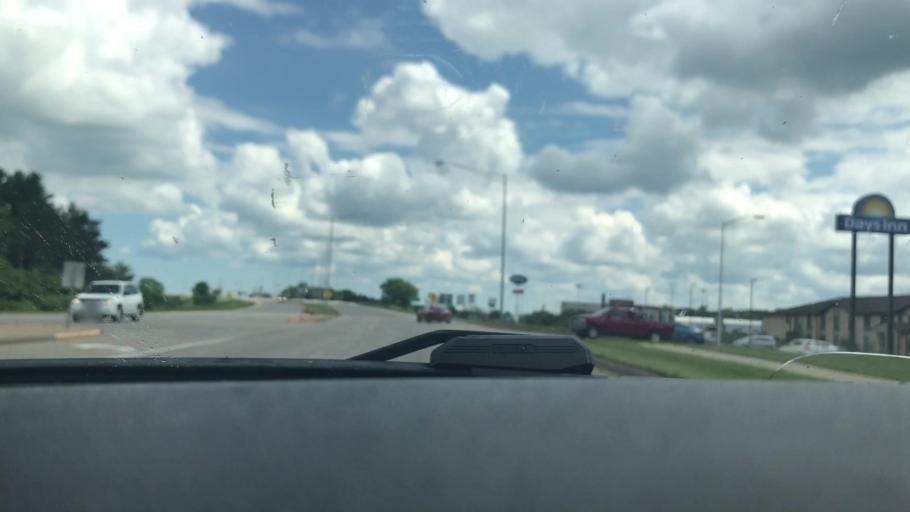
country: US
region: Wisconsin
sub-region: Jackson County
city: Black River Falls
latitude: 44.2944
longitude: -90.8290
